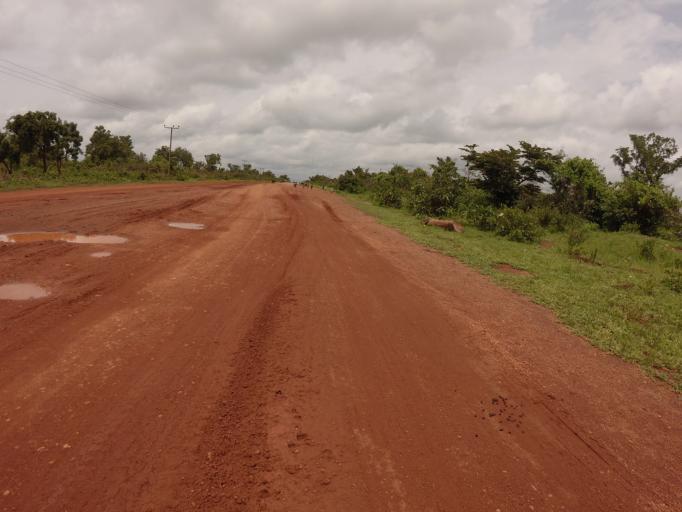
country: GH
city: Kpandae
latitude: 8.4519
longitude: 0.3477
